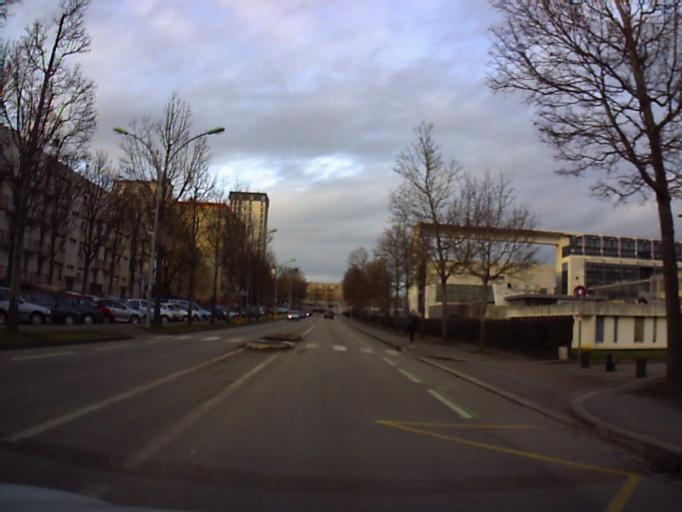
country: FR
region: Brittany
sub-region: Departement d'Ille-et-Vilaine
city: Rennes
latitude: 48.1193
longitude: -1.7046
